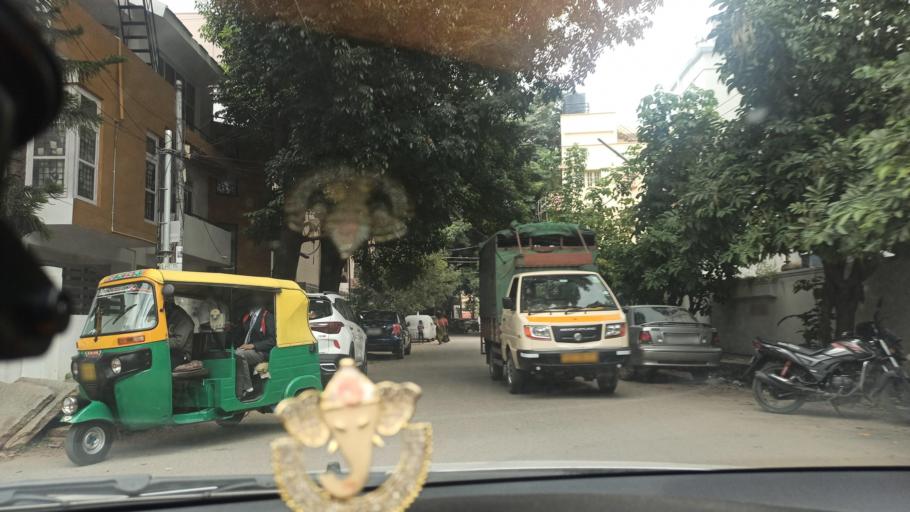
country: IN
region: Karnataka
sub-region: Bangalore Urban
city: Bangalore
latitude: 12.9182
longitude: 77.6470
